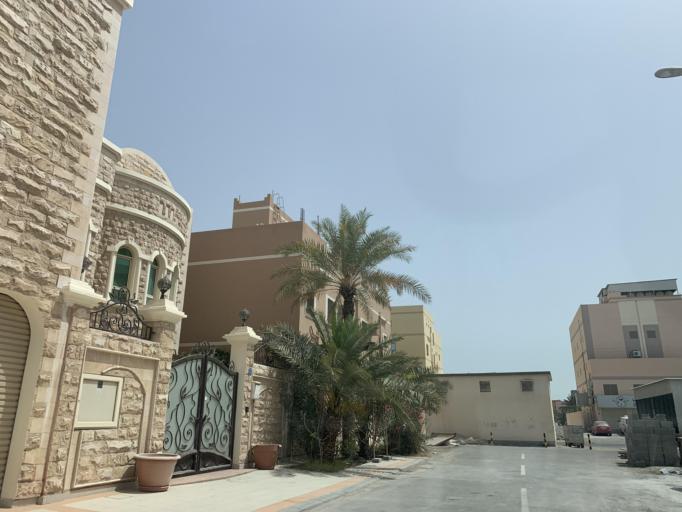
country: BH
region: Northern
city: Sitrah
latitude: 26.1402
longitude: 50.6009
